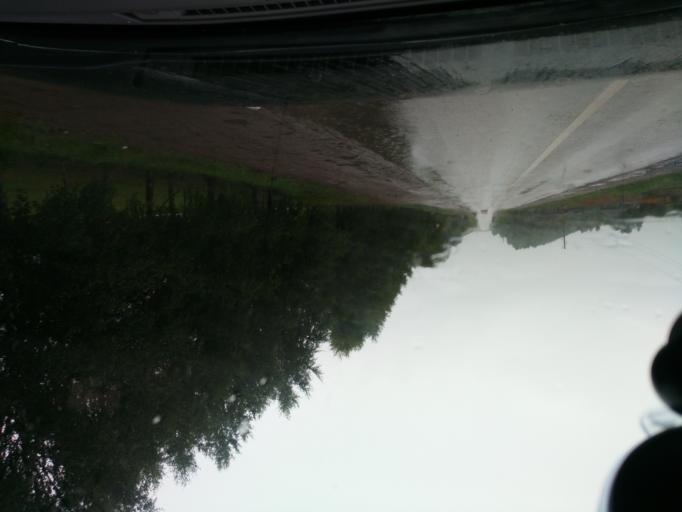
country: RU
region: Perm
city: Osa
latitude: 57.1873
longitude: 55.5909
